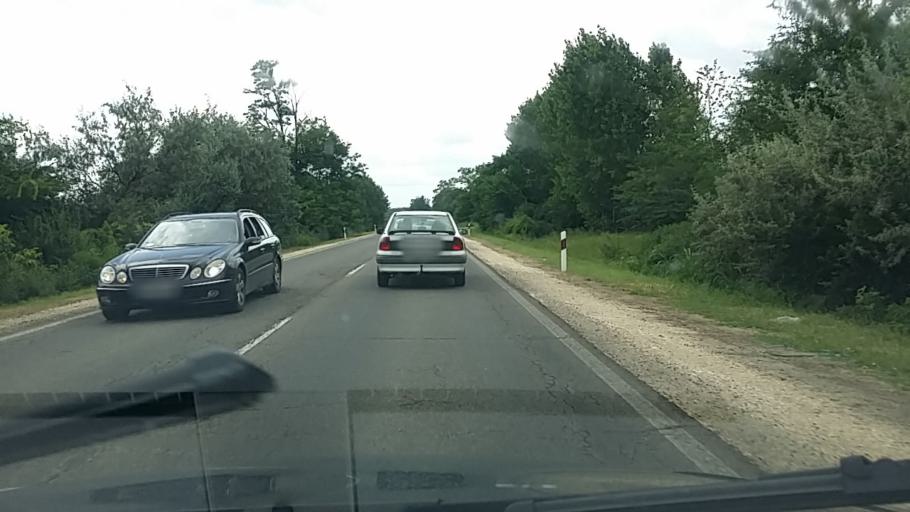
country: HU
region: Pest
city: Orkeny
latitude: 47.1390
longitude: 19.4060
